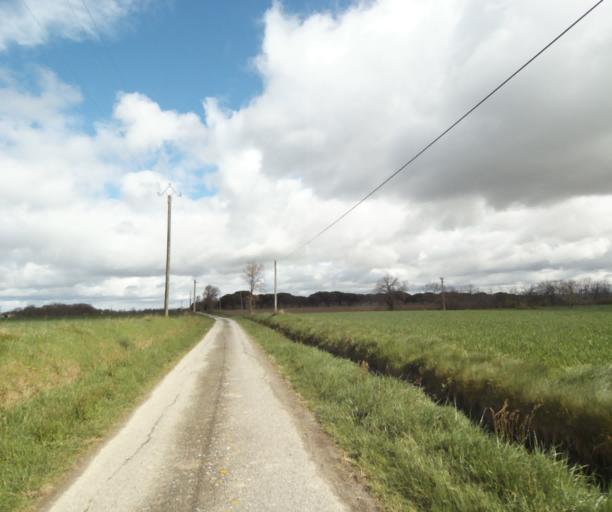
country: FR
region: Midi-Pyrenees
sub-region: Departement de l'Ariege
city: Saverdun
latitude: 43.2348
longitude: 1.5488
